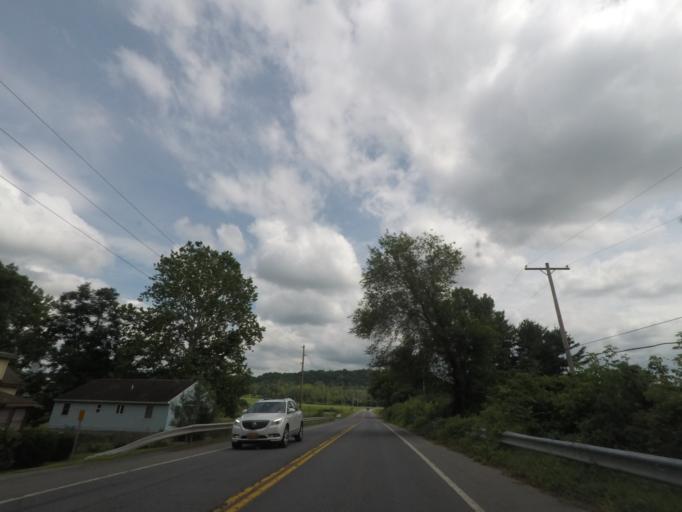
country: US
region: New York
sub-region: Saratoga County
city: Stillwater
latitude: 42.9365
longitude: -73.6488
